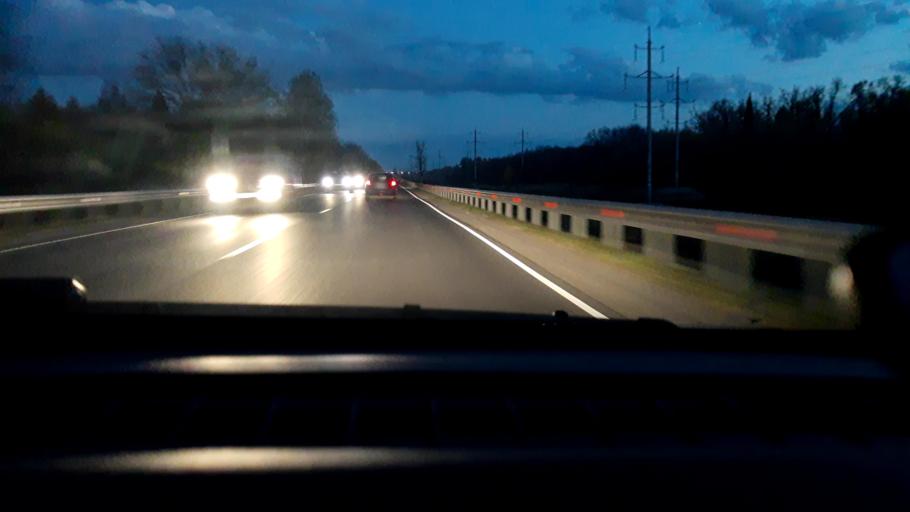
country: RU
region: Nizjnij Novgorod
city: Lukino
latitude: 56.4657
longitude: 43.6179
